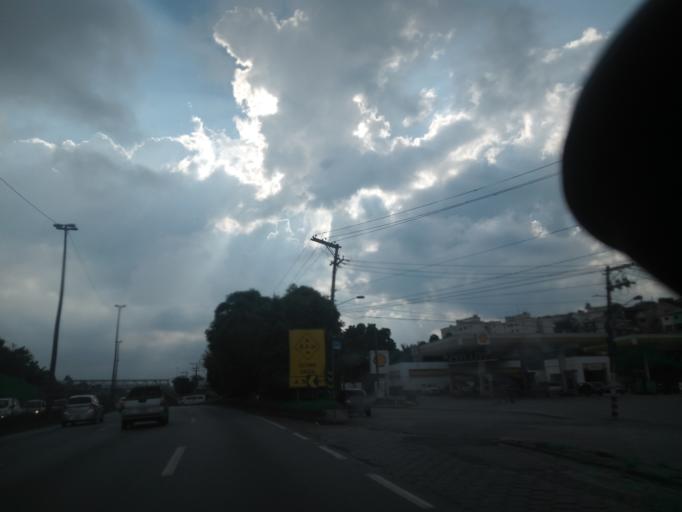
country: BR
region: Sao Paulo
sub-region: Taboao Da Serra
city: Taboao da Serra
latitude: -23.6078
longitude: -46.7673
